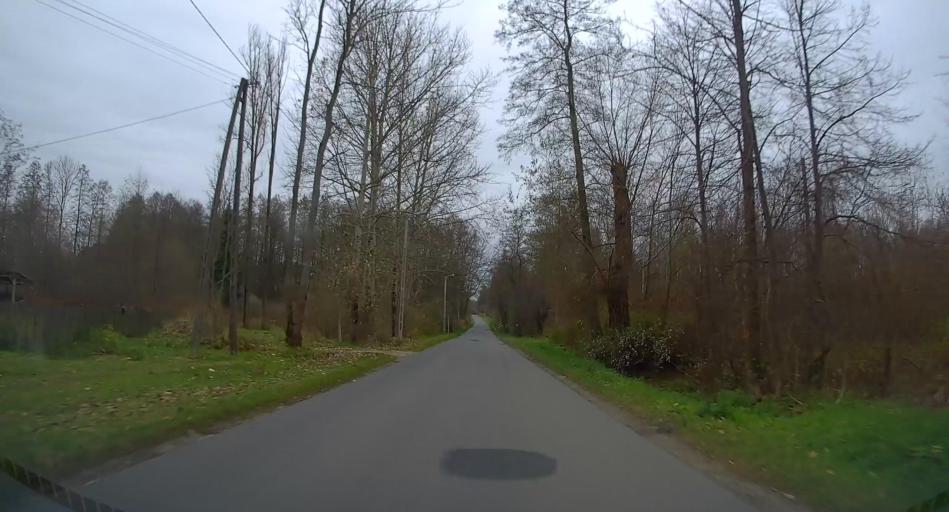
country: PL
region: Lodz Voivodeship
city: Zabia Wola
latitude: 51.9876
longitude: 20.6600
